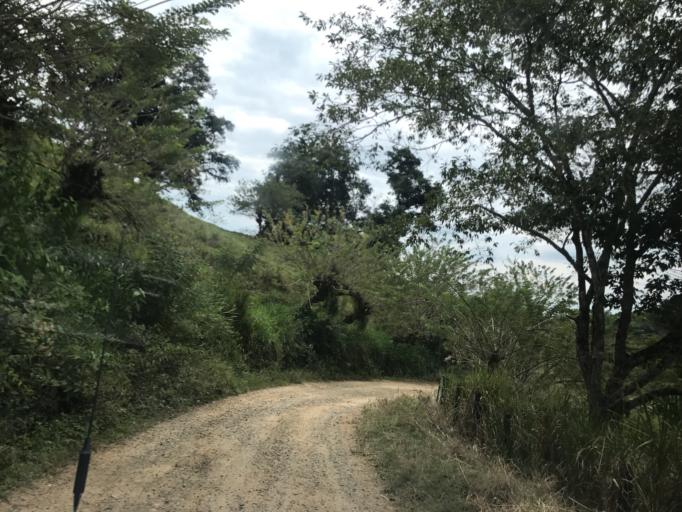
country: CO
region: Valle del Cauca
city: Obando
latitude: 4.5625
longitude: -75.9342
